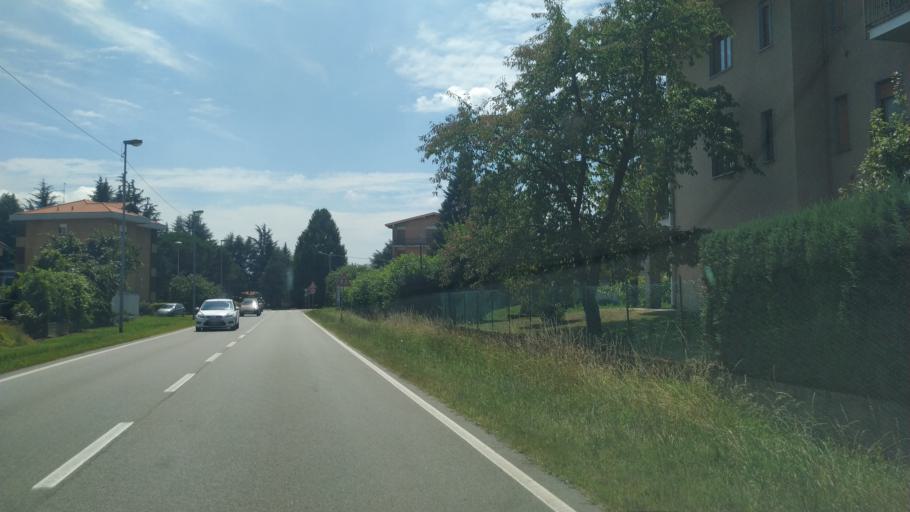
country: IT
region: Piedmont
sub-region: Provincia di Novara
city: Borgomanero
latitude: 45.6902
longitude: 8.4560
